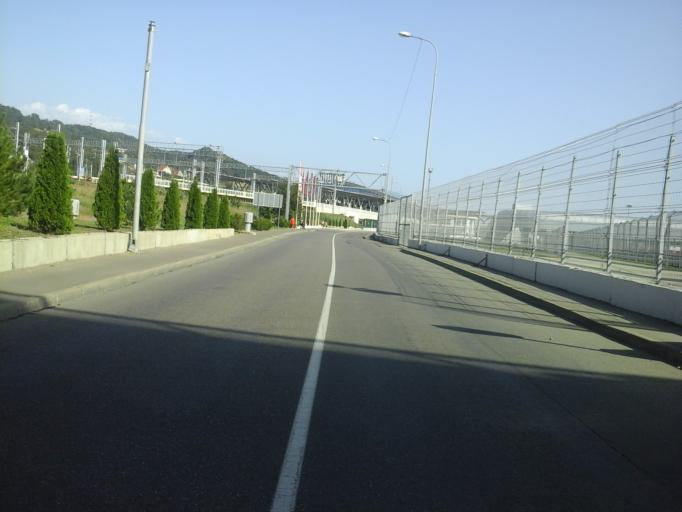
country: RU
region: Krasnodarskiy
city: Adler
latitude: 43.4133
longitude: 39.9684
